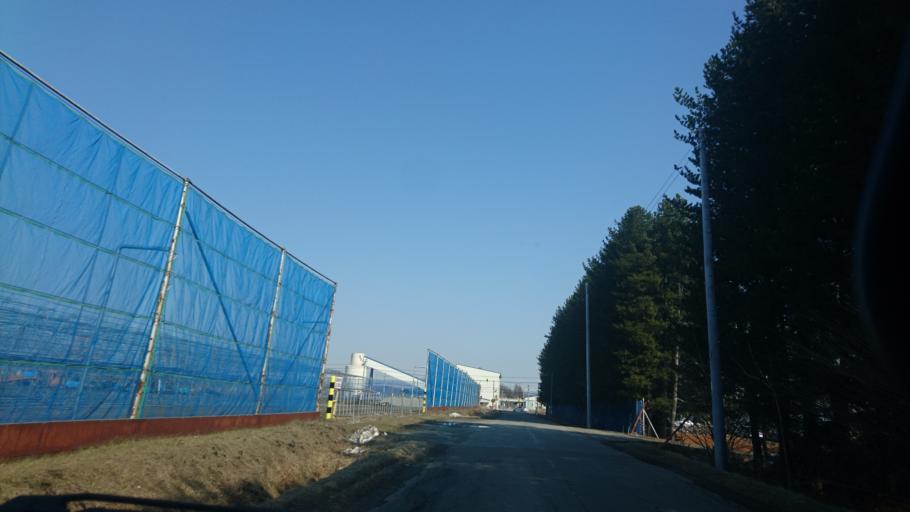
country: JP
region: Hokkaido
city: Obihiro
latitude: 42.9189
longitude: 143.0761
